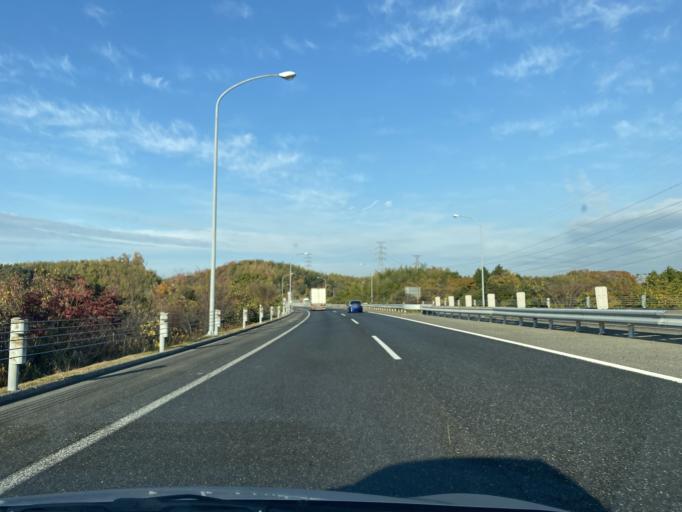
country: JP
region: Osaka
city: Izumi
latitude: 34.4095
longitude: 135.4477
